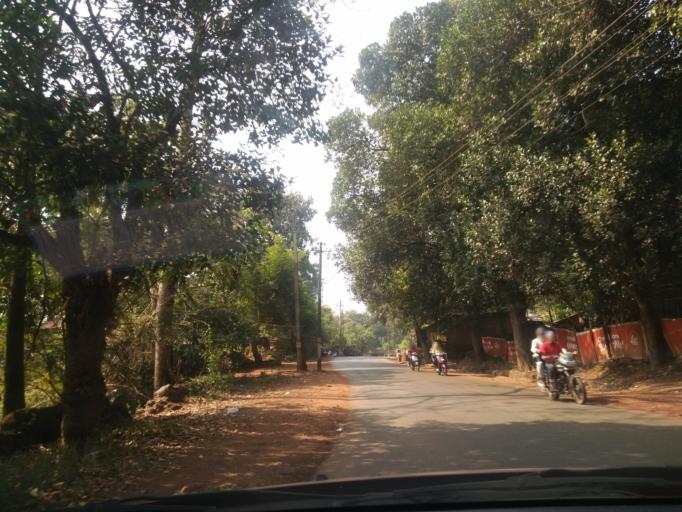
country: IN
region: Goa
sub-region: North Goa
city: Sanquelim
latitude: 15.5425
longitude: 74.0601
